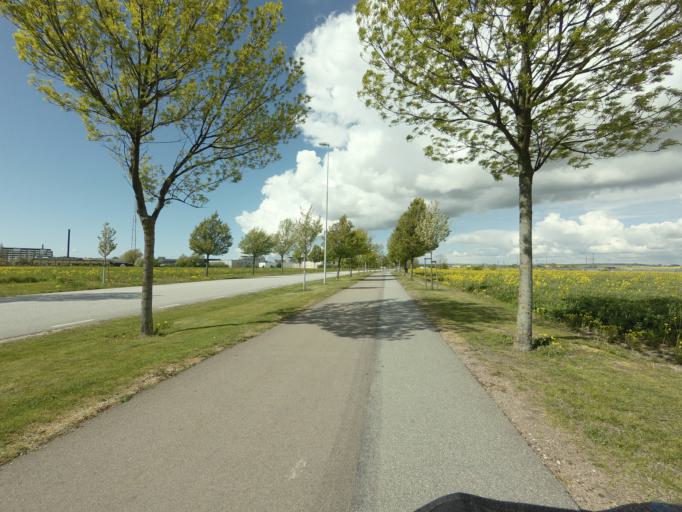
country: SE
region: Skane
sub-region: Landskrona
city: Landskrona
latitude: 55.8850
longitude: 12.8542
